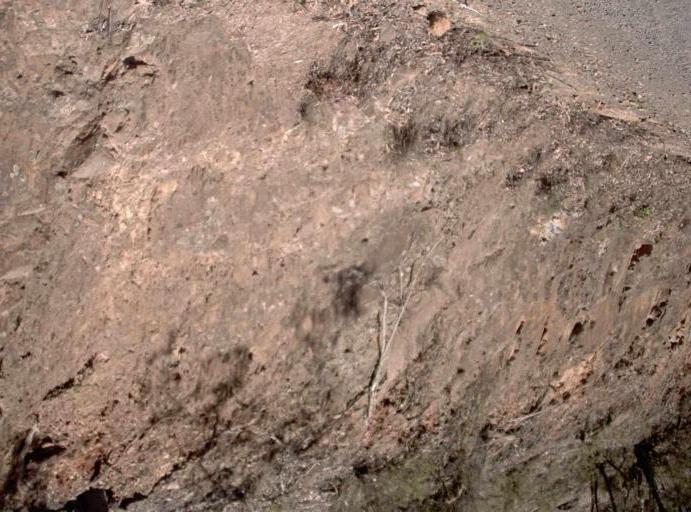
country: AU
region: New South Wales
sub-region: Bombala
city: Bombala
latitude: -37.0986
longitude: 148.6322
